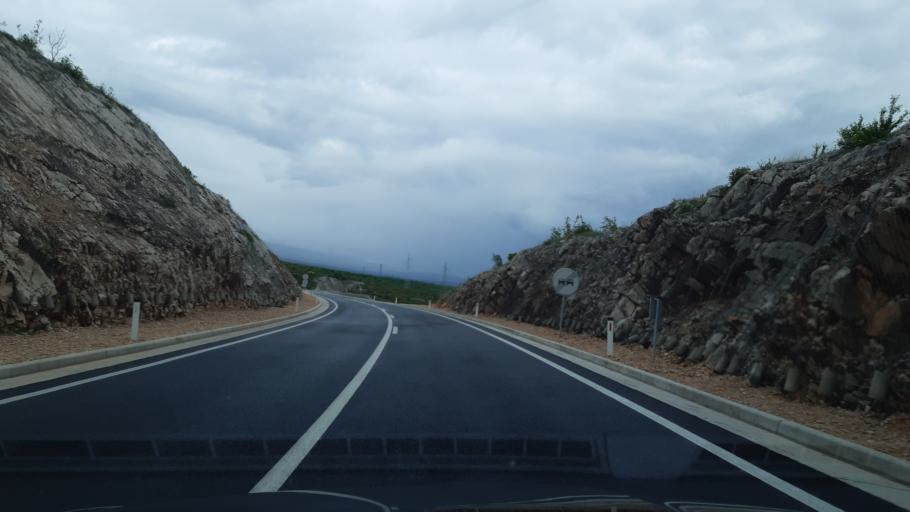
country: BA
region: Federation of Bosnia and Herzegovina
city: Ilici
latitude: 43.3238
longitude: 17.7417
